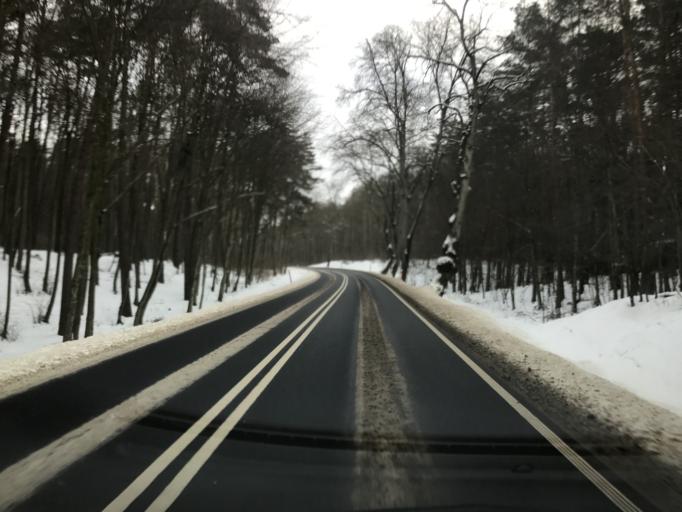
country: PL
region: Warmian-Masurian Voivodeship
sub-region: Powiat dzialdowski
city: Lidzbark
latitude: 53.3155
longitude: 19.8139
